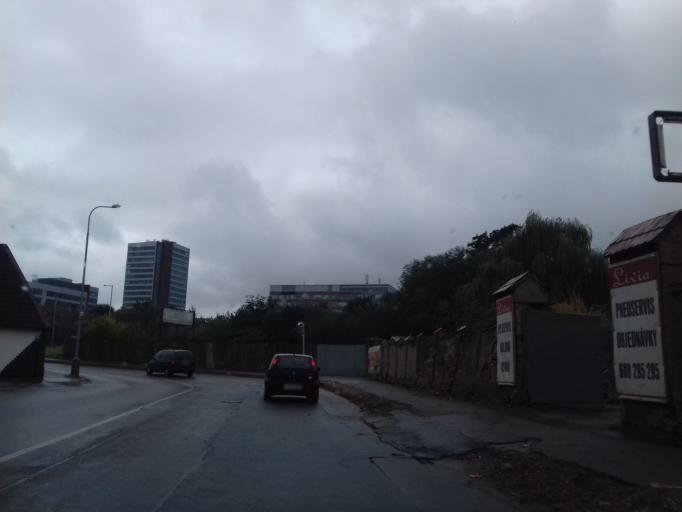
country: CZ
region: Praha
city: Branik
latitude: 50.0528
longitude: 14.3567
